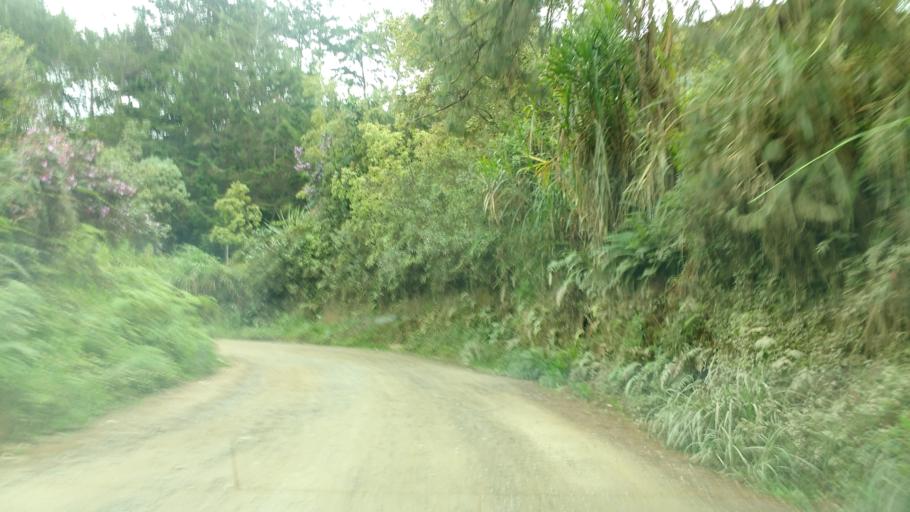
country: CO
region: Antioquia
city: San Vicente
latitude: 6.3090
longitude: -75.3230
